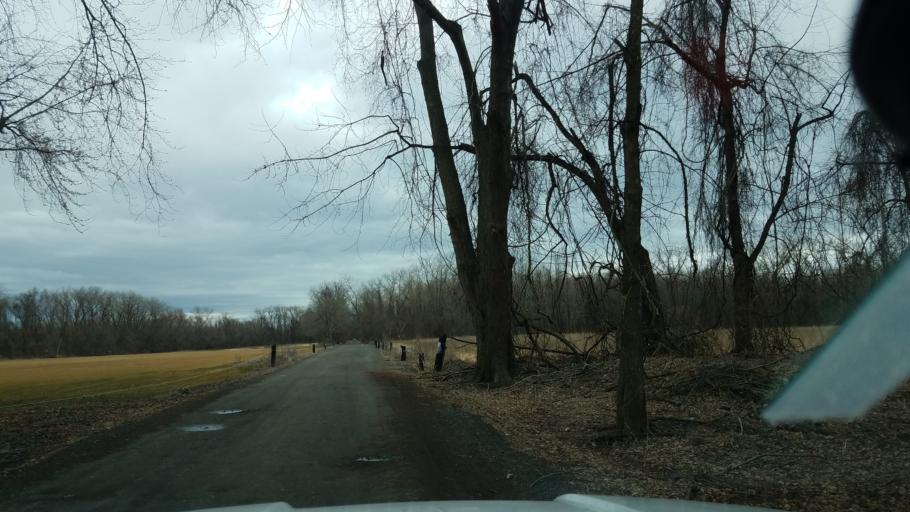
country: US
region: Connecticut
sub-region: Hartford County
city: Wethersfield
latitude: 41.7090
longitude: -72.6398
